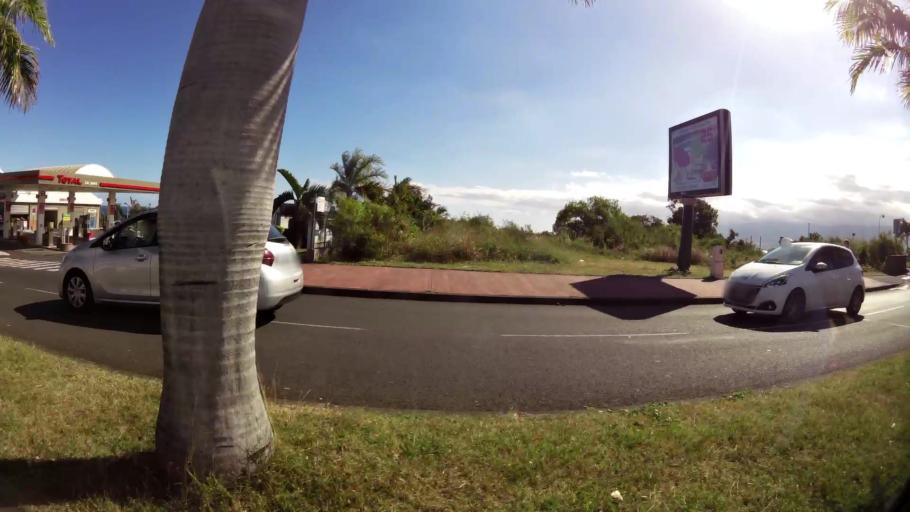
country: RE
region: Reunion
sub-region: Reunion
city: Saint-Pierre
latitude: -21.3307
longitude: 55.4723
